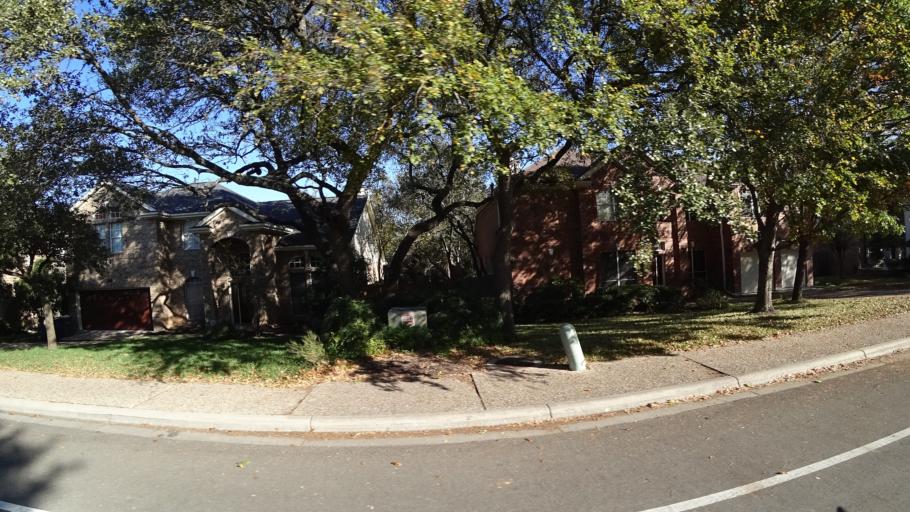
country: US
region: Texas
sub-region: Williamson County
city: Jollyville
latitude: 30.4188
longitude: -97.7789
